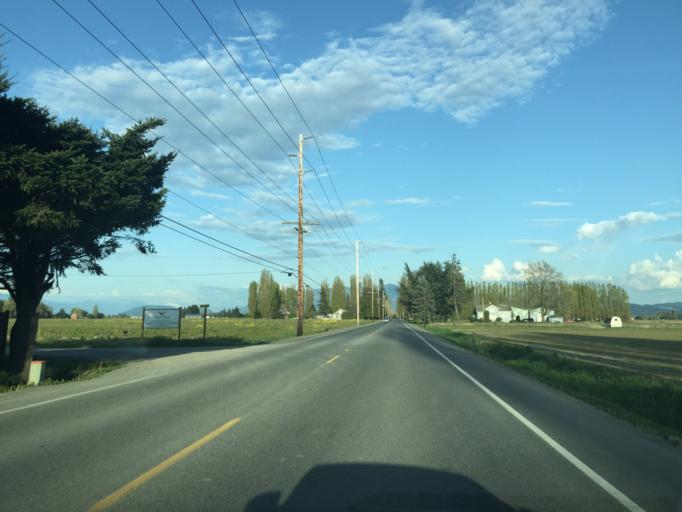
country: US
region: Washington
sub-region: Skagit County
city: Mount Vernon
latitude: 48.4208
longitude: -122.4166
